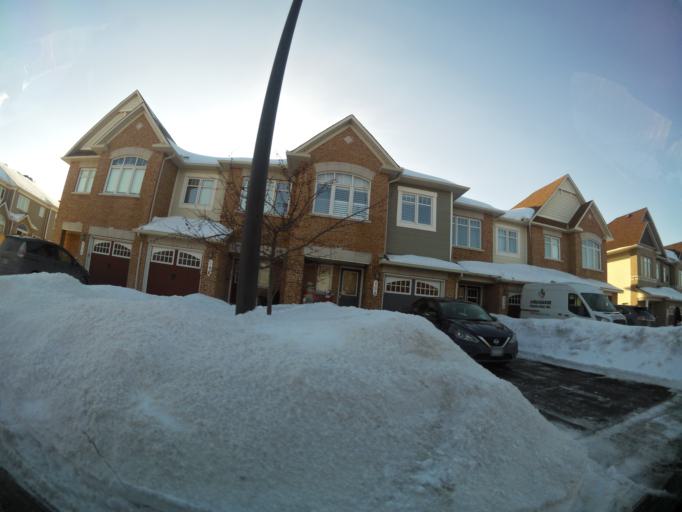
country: CA
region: Ontario
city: Ottawa
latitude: 45.4326
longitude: -75.5142
